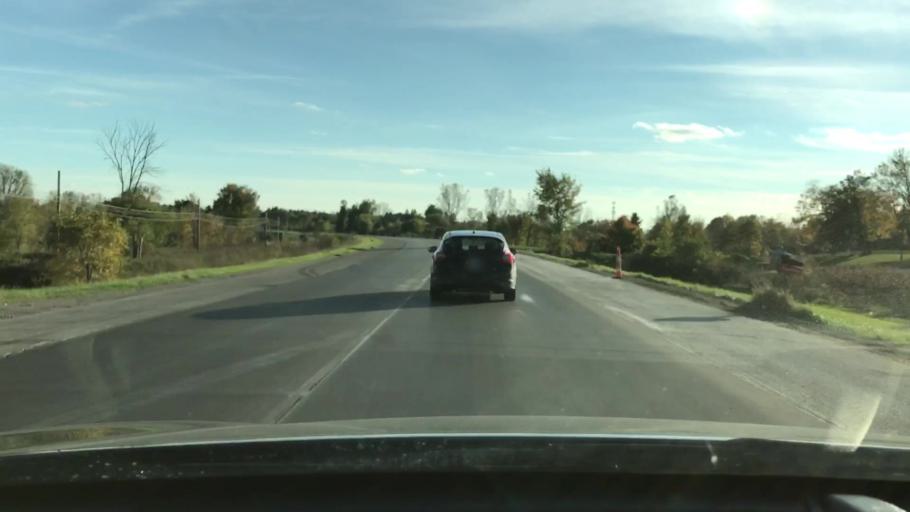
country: US
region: Michigan
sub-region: Shiawassee County
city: Owosso
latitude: 42.9452
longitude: -84.2215
